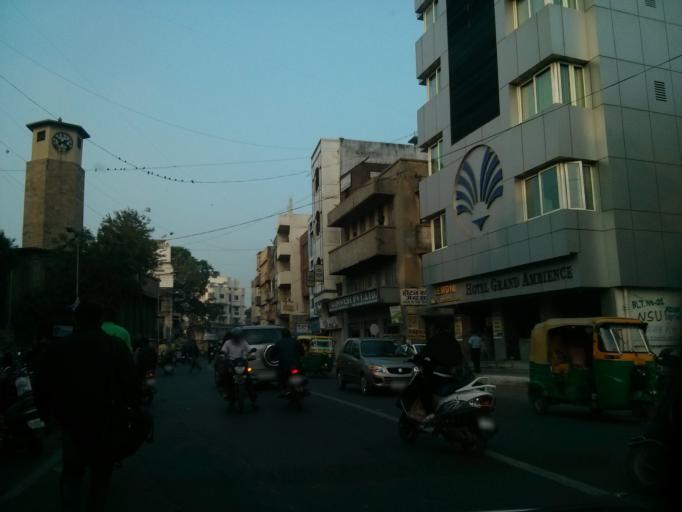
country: IN
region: Gujarat
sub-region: Ahmadabad
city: Ahmedabad
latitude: 23.0277
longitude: 72.5813
